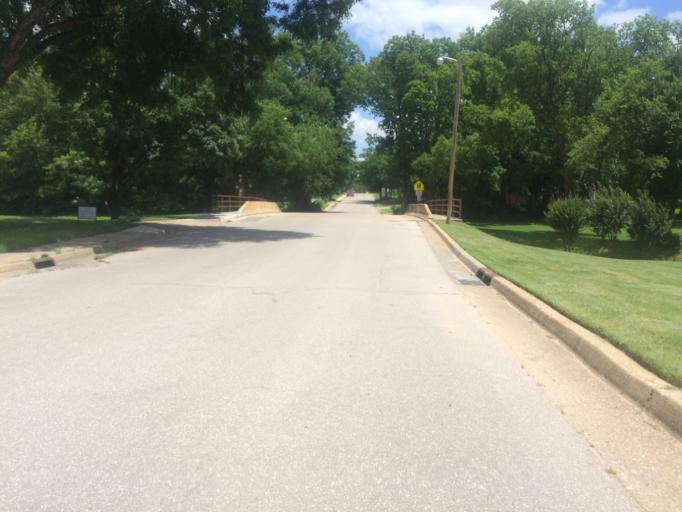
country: US
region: Oklahoma
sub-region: Cleveland County
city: Norman
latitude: 35.2075
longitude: -97.4570
